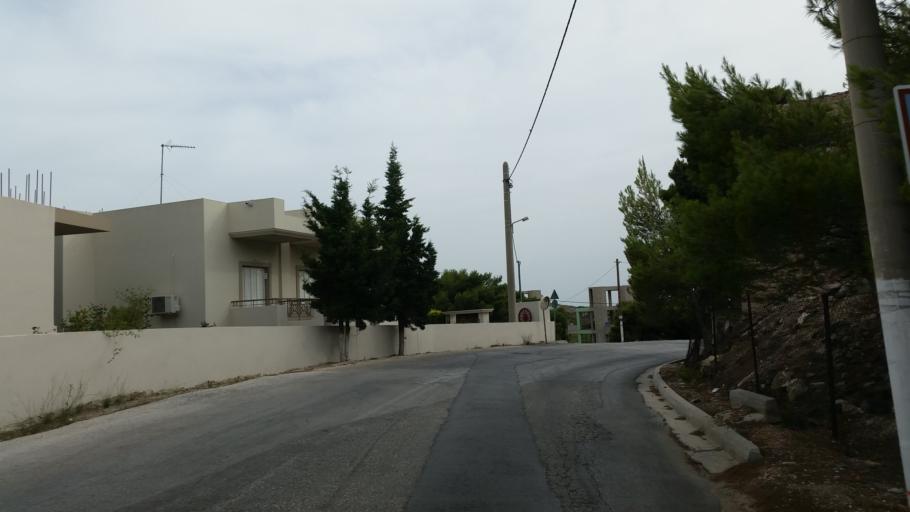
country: GR
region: Attica
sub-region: Nomarchia Anatolikis Attikis
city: Lavrio
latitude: 37.7244
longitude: 24.0140
